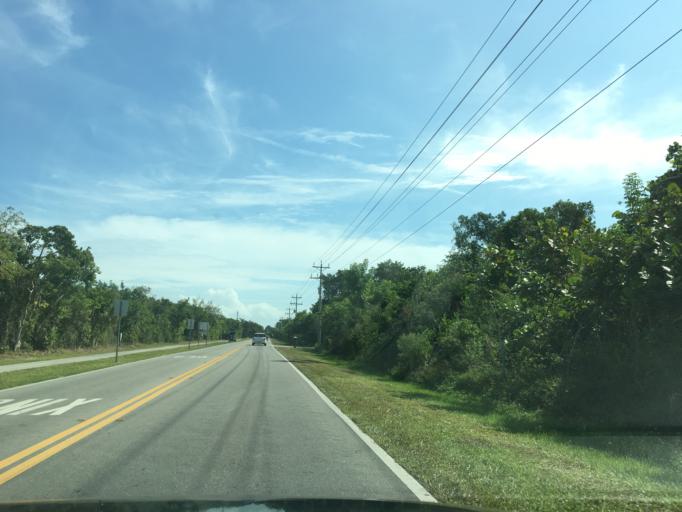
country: US
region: Florida
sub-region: Lee County
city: Saint James City
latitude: 26.4396
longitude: -82.0980
